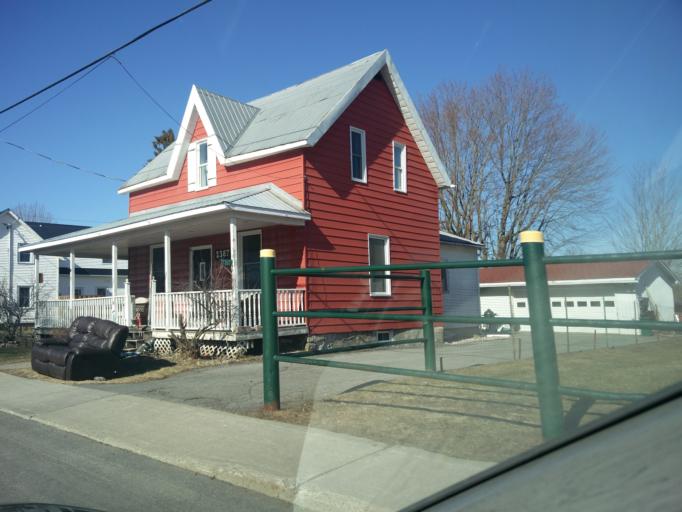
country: CA
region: Ontario
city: Bells Corners
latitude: 45.1269
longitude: -75.7178
